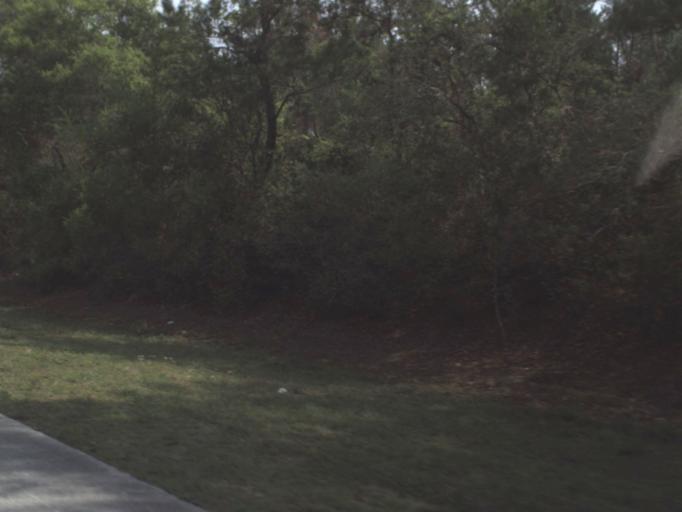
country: US
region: Florida
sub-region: Lake County
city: Astor
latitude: 29.2526
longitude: -81.6463
